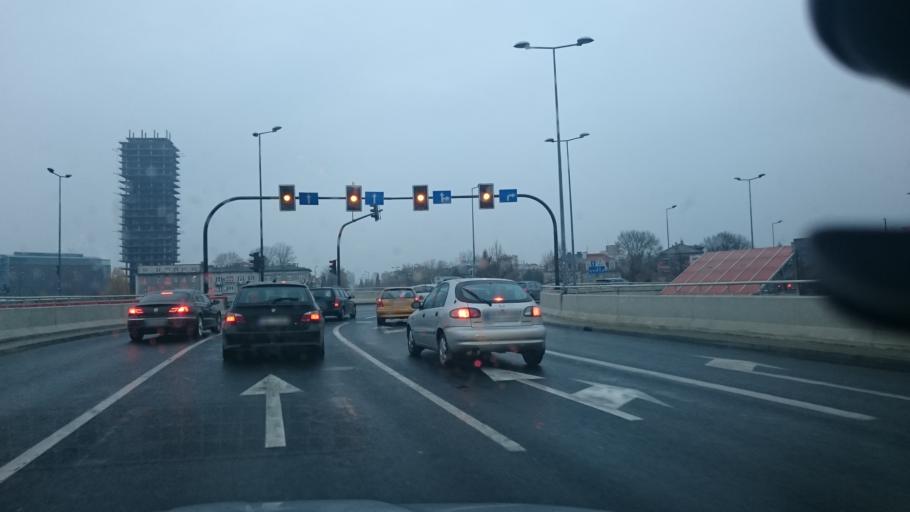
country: PL
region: Lesser Poland Voivodeship
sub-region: Krakow
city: Krakow
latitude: 50.0648
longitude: 19.9597
